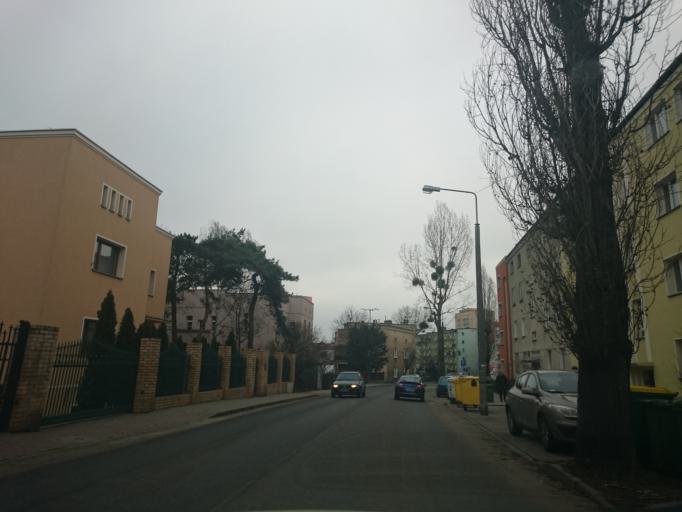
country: PL
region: Kujawsko-Pomorskie
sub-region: Torun
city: Torun
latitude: 53.0132
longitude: 18.5904
